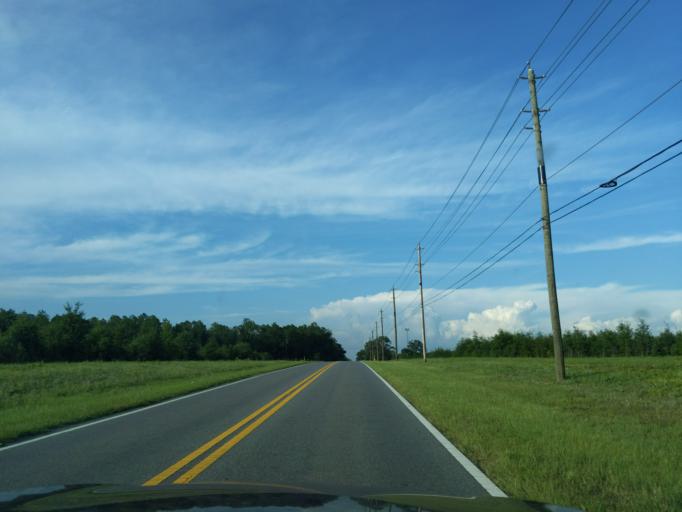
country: US
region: Florida
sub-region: Leon County
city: Tallahassee
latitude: 30.3963
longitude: -84.3184
